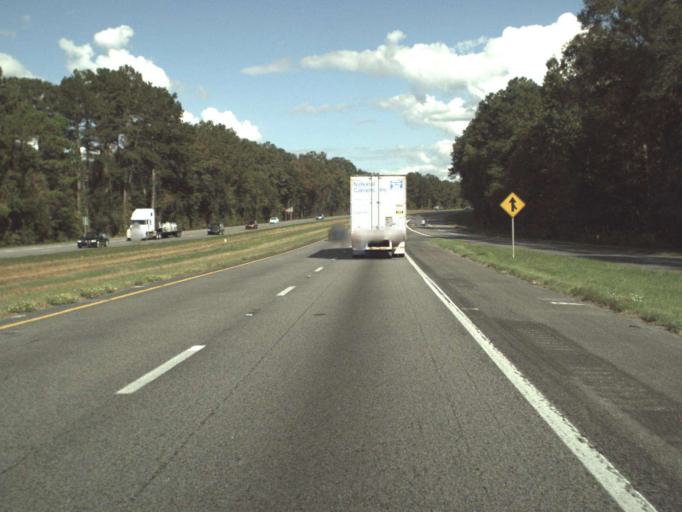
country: US
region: Florida
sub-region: Jefferson County
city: Monticello
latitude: 30.4884
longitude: -84.0220
